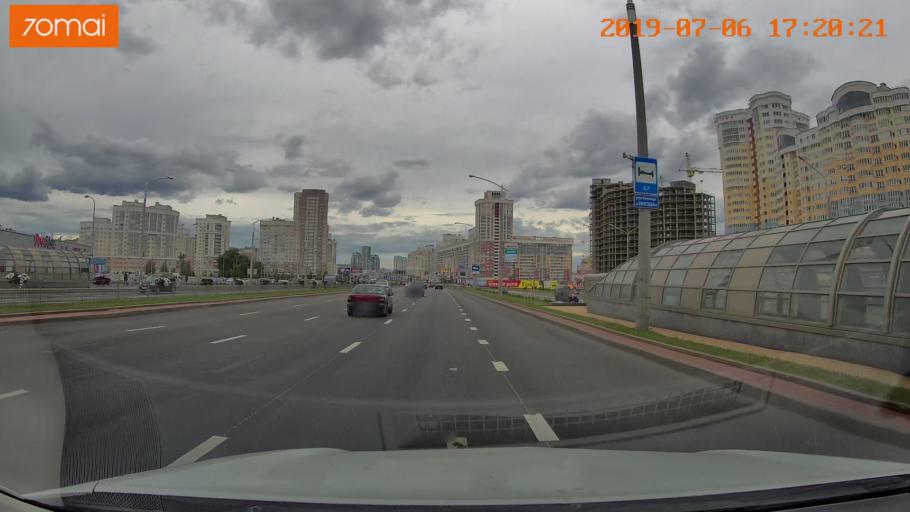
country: BY
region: Minsk
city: Shchomyslitsa
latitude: 53.8428
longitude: 27.4761
